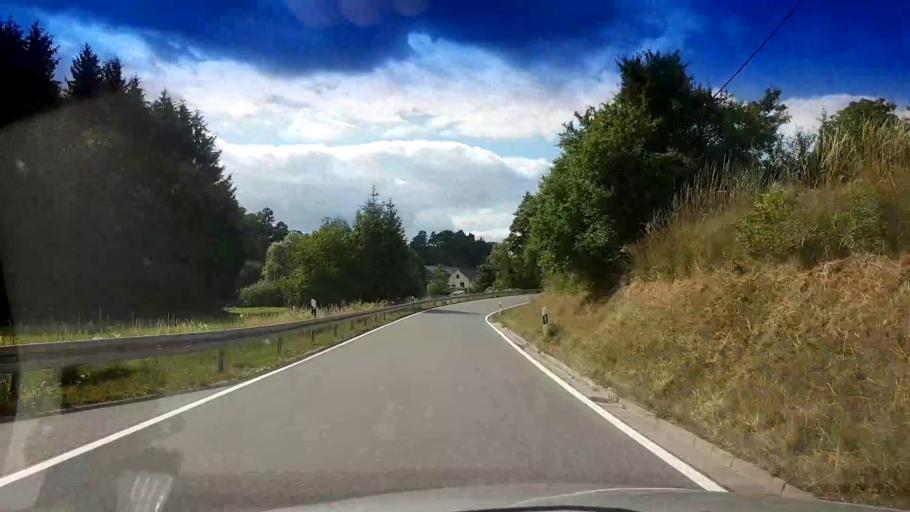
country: DE
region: Bavaria
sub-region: Upper Franconia
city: Lauter
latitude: 49.9887
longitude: 10.7599
